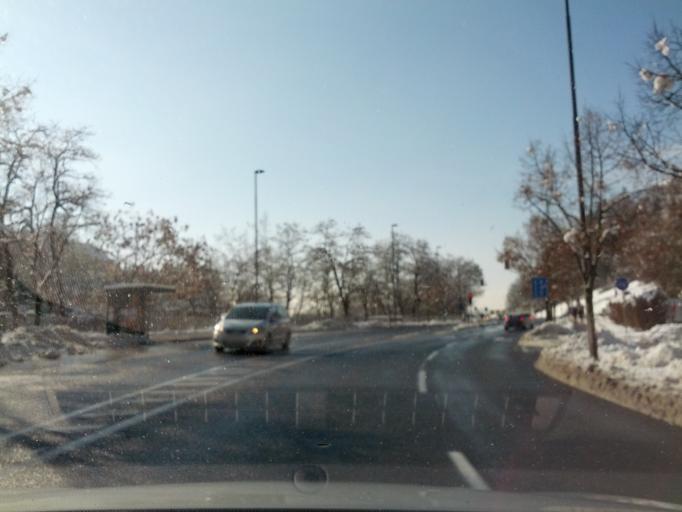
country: SI
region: Ljubljana
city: Ljubljana
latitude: 46.0452
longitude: 14.5186
